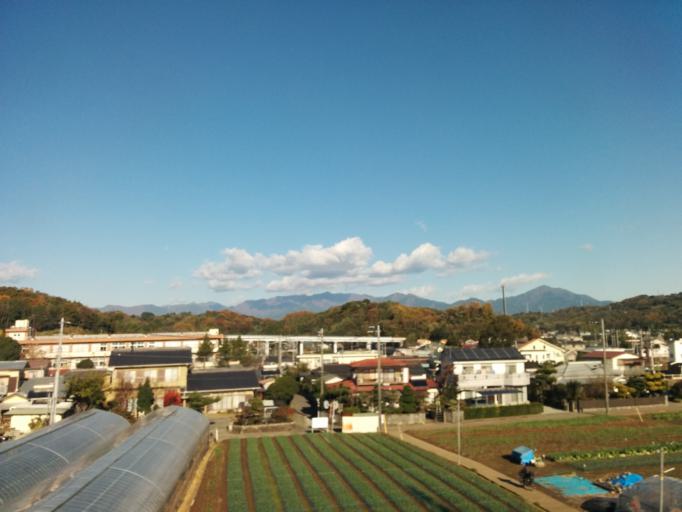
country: JP
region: Kanagawa
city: Ninomiya
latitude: 35.3007
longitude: 139.2262
